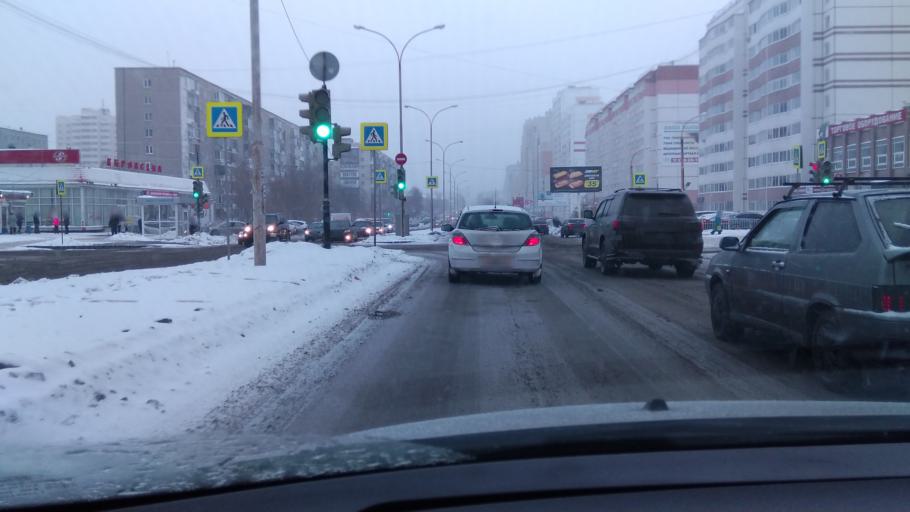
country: RU
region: Sverdlovsk
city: Yekaterinburg
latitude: 56.9079
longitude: 60.5909
